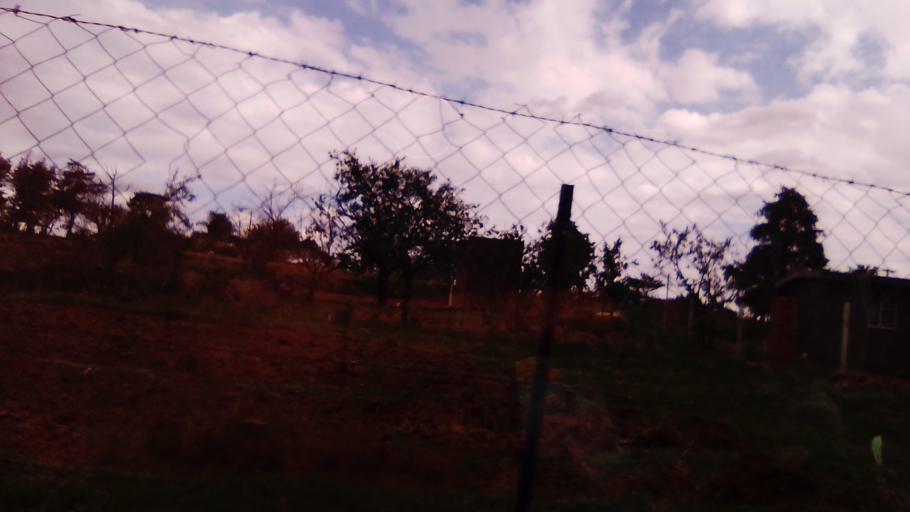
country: LS
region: Berea
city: Teyateyaneng
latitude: -29.3335
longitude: 27.7081
